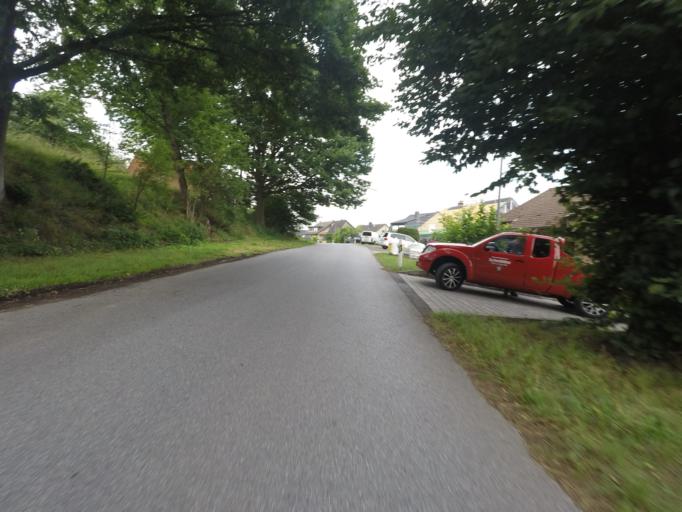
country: DE
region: North Rhine-Westphalia
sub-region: Regierungsbezirk Detmold
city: Herford
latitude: 52.0864
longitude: 8.6228
